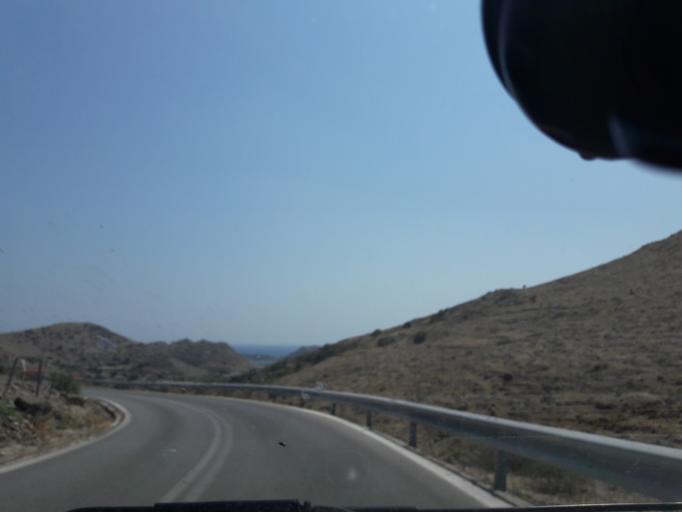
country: GR
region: North Aegean
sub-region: Nomos Lesvou
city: Myrina
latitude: 39.8601
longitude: 25.0813
